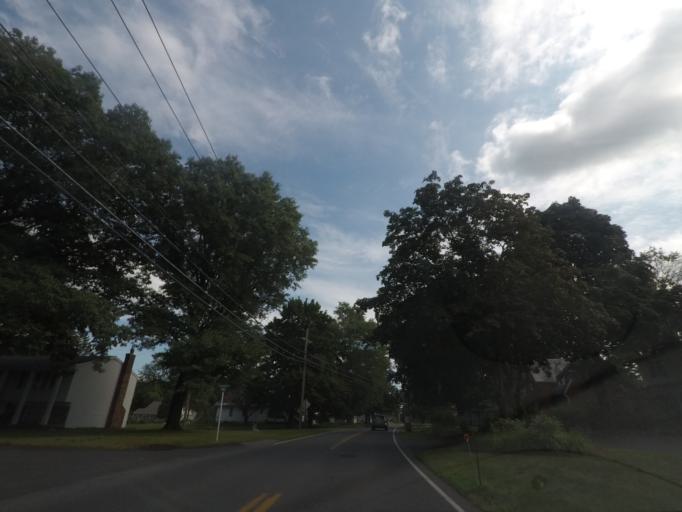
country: US
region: New York
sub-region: Albany County
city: Delmar
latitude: 42.6235
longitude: -73.8076
